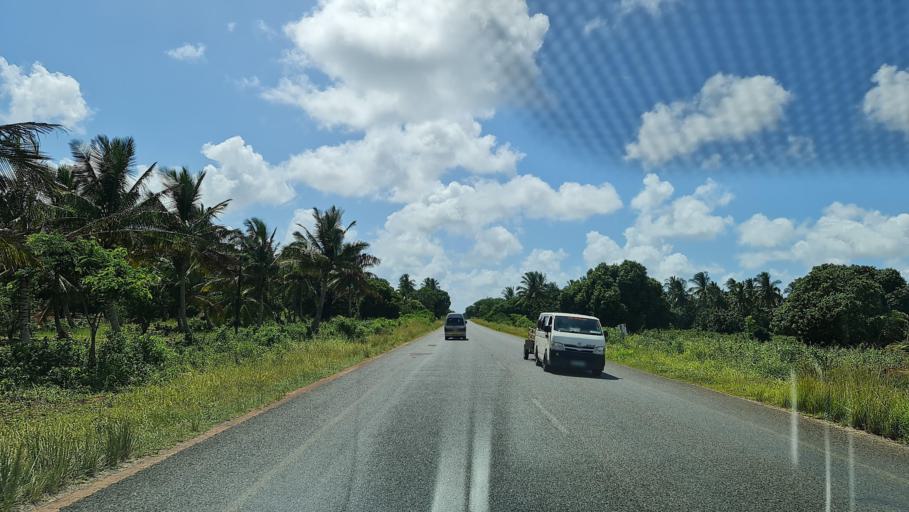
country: MZ
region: Inhambane
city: Maxixe
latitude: -24.5413
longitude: 34.9136
